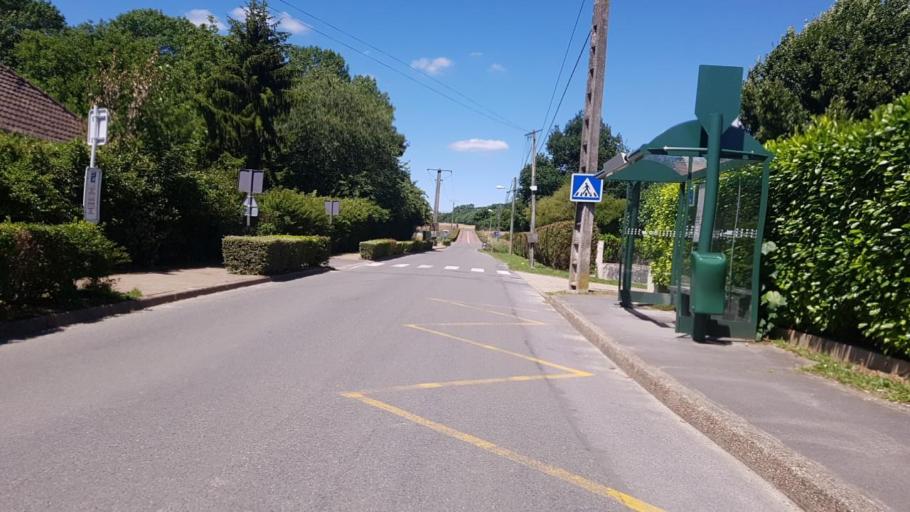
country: FR
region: Ile-de-France
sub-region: Departement de Seine-et-Marne
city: Sammeron
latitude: 48.9558
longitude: 3.0667
